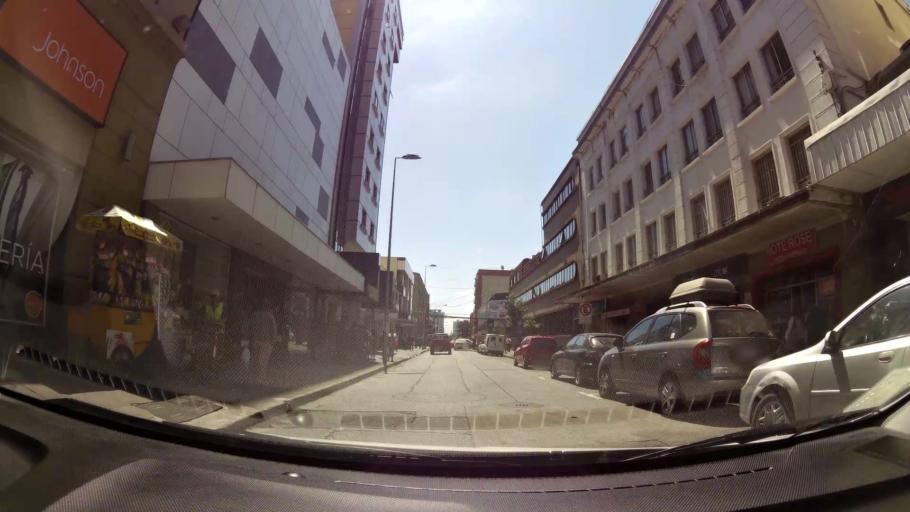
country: CL
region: Biobio
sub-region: Provincia de Concepcion
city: Concepcion
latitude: -36.8253
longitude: -73.0490
